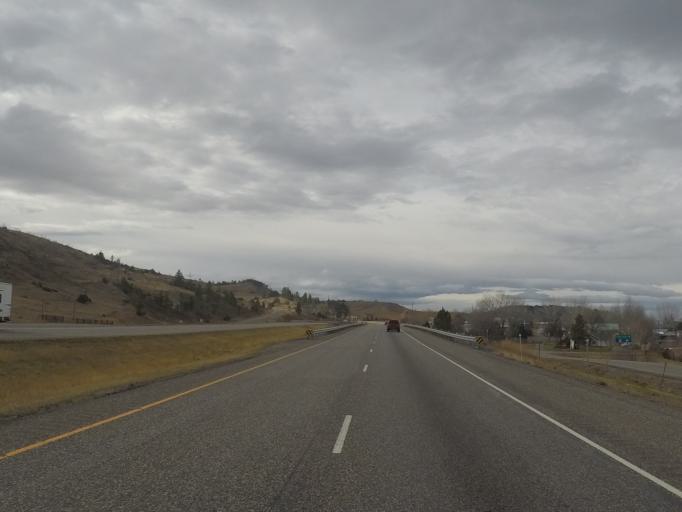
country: US
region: Montana
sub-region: Stillwater County
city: Absarokee
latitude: 45.7056
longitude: -109.5393
